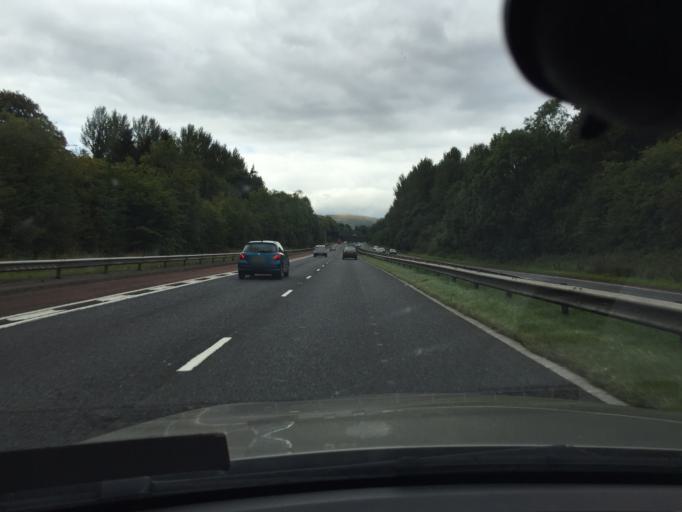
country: GB
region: Northern Ireland
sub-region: Lisburn District
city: Lisburn
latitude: 54.5457
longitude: -5.9942
